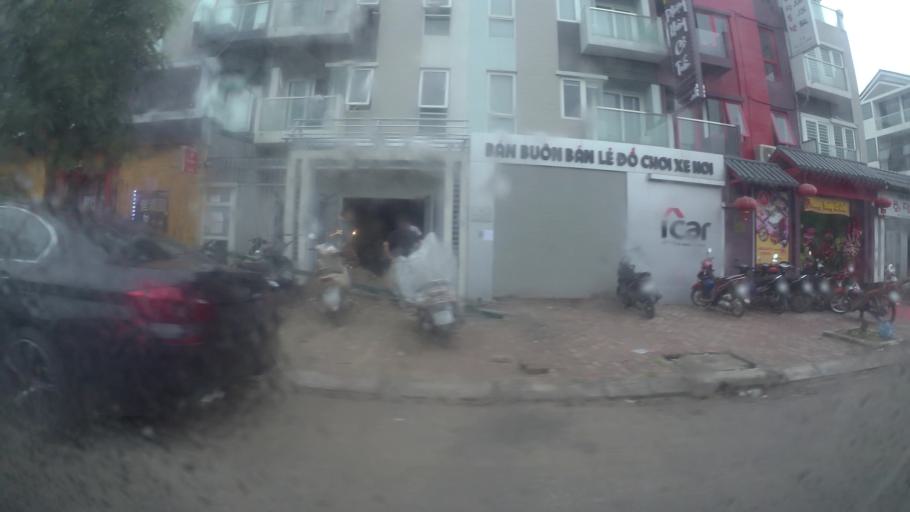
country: VN
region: Ha Noi
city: Cau Giay
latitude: 21.0199
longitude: 105.7876
